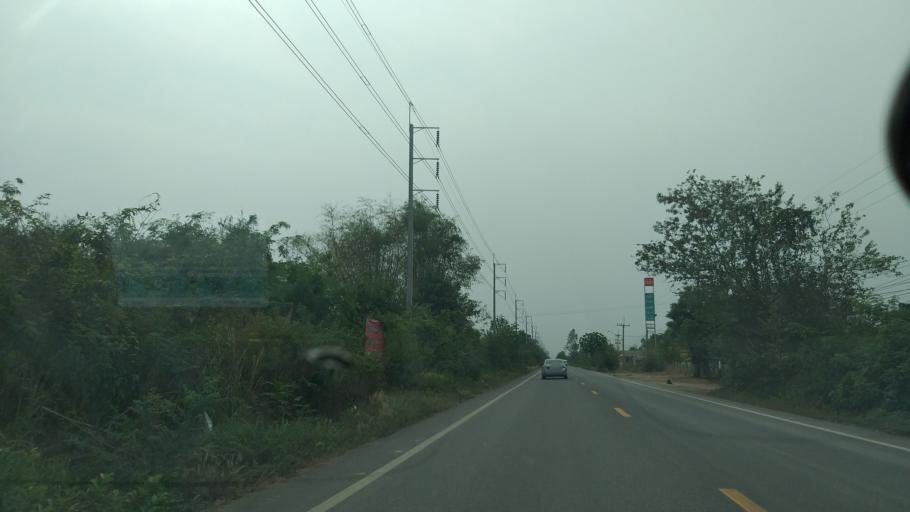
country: TH
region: Chachoengsao
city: Plaeng Yao
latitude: 13.5804
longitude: 101.2322
